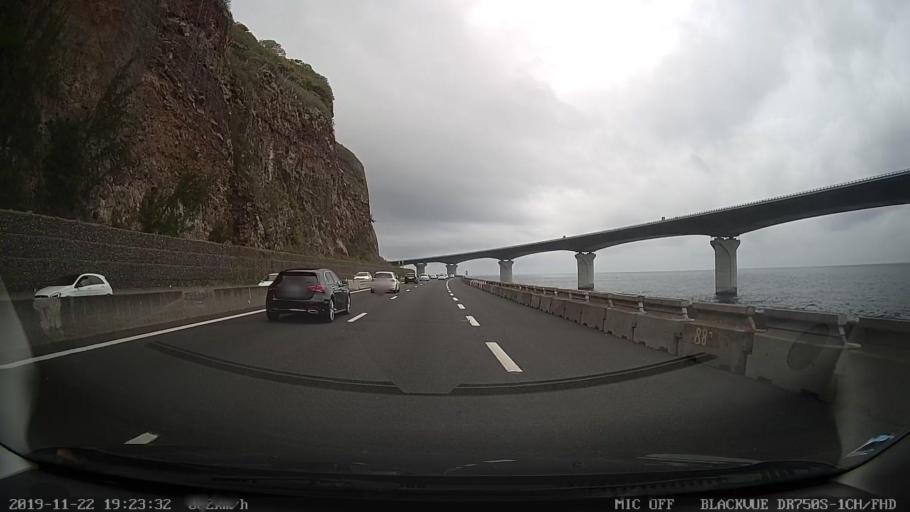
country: RE
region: Reunion
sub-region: Reunion
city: Saint-Denis
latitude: -20.8808
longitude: 55.3983
